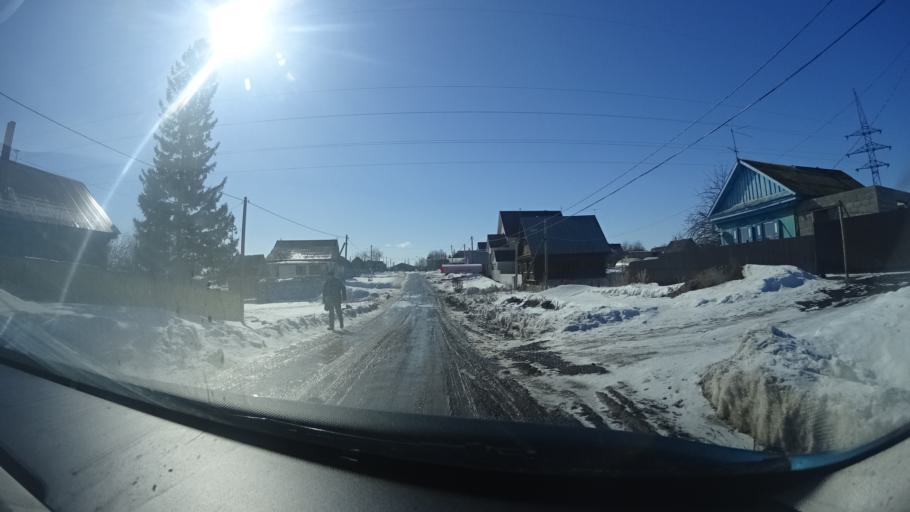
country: RU
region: Bashkortostan
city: Chishmy
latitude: 54.5788
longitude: 55.3784
